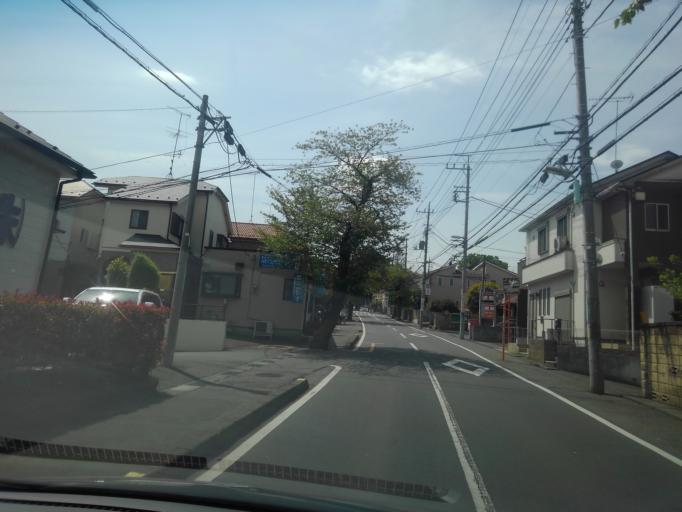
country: JP
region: Saitama
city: Tokorozawa
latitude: 35.7867
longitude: 139.4393
